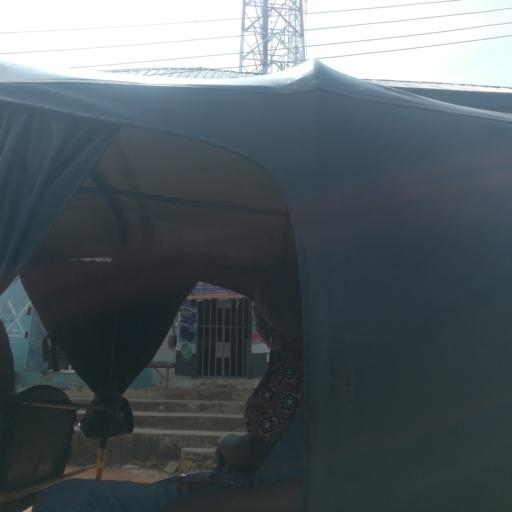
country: NG
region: Plateau
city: Jos
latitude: 9.9277
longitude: 8.8567
